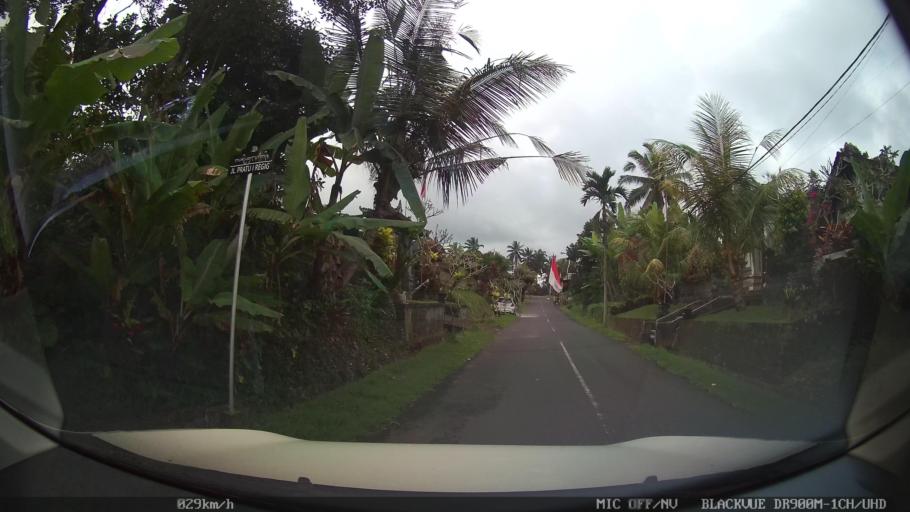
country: ID
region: Bali
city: Badung
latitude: -8.4286
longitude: 115.2261
